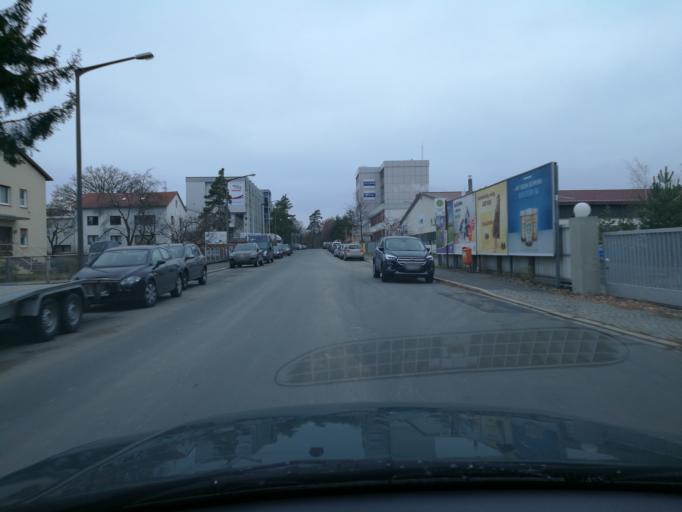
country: DE
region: Bavaria
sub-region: Regierungsbezirk Mittelfranken
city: Feucht
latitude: 49.4150
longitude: 11.1661
